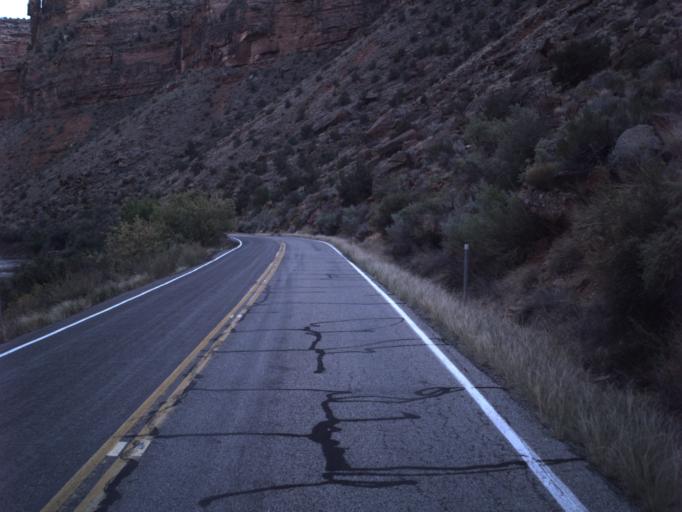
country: US
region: Utah
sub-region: Grand County
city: Moab
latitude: 38.7965
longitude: -109.3308
